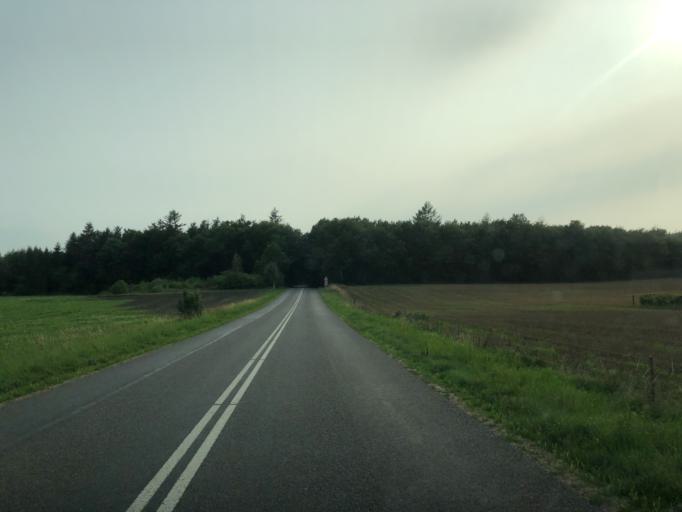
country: DK
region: Central Jutland
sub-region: Ringkobing-Skjern Kommune
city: Videbaek
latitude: 56.0656
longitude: 8.6905
